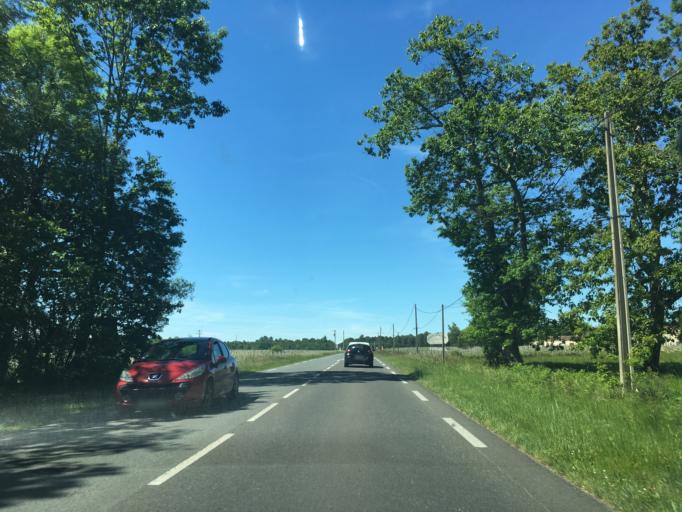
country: FR
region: Aquitaine
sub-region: Departement de la Gironde
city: Saint-Sauveur
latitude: 45.1673
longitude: -0.8335
